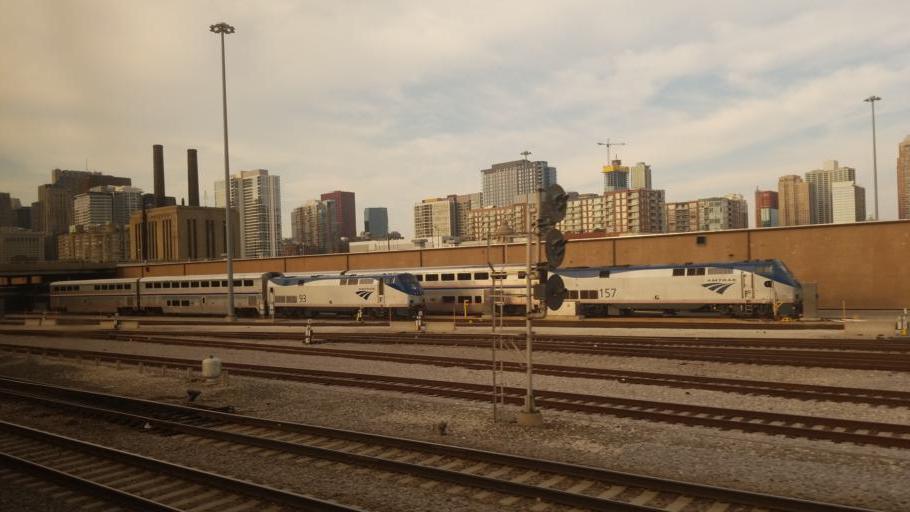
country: US
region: Illinois
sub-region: Cook County
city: Chicago
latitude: 41.8658
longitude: -87.6374
